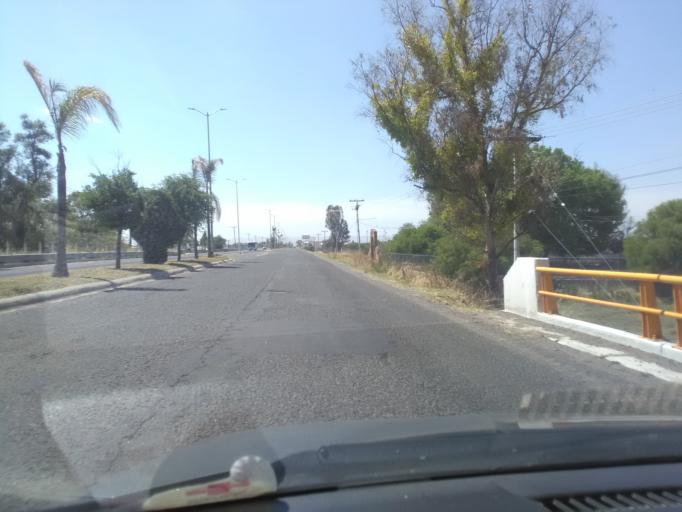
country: MX
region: Durango
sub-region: Durango
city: Jose Refugio Salcido
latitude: 24.0257
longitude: -104.5675
